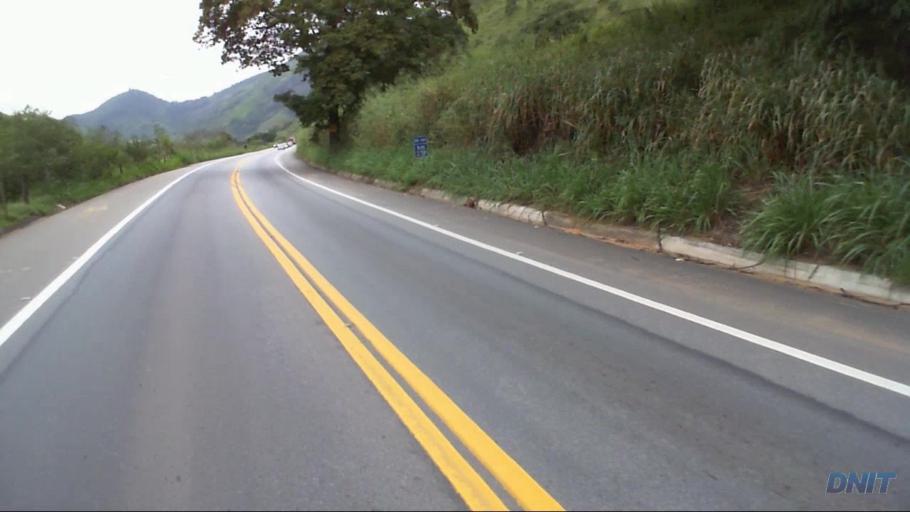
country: BR
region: Minas Gerais
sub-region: Timoteo
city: Timoteo
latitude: -19.5813
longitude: -42.7269
